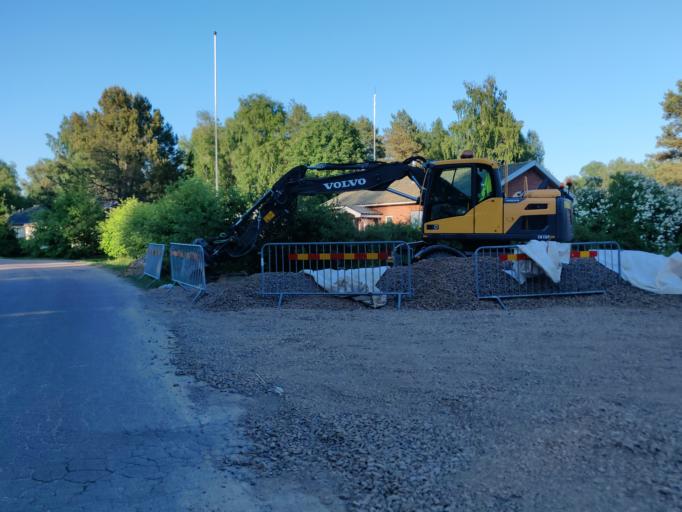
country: SE
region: Vaermland
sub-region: Hagfors Kommun
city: Hagfors
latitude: 60.0037
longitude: 13.5919
